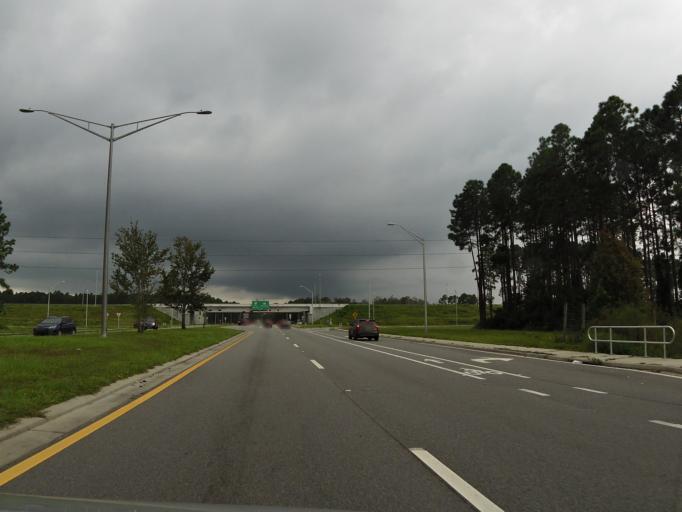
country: US
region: Florida
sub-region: Clay County
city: Bellair-Meadowbrook Terrace
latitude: 30.1959
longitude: -81.8352
